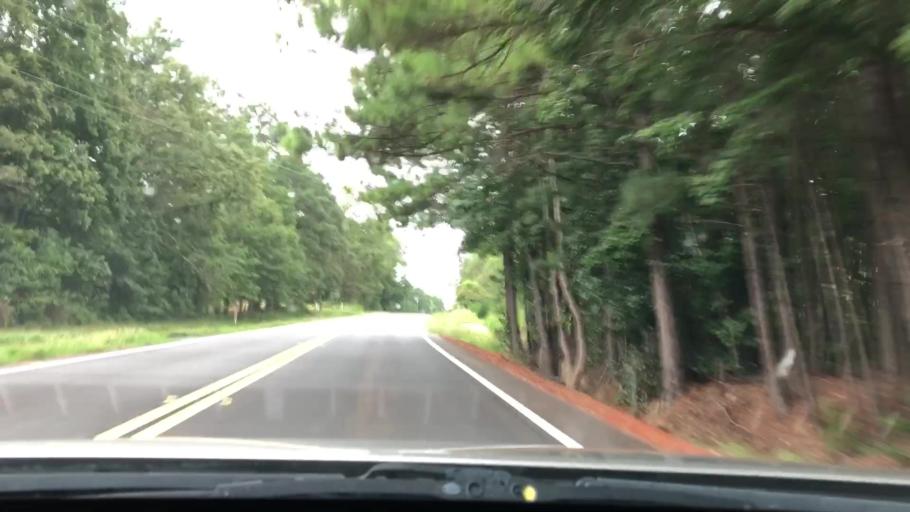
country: US
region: Georgia
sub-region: Pike County
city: Zebulon
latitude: 33.0209
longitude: -84.3993
